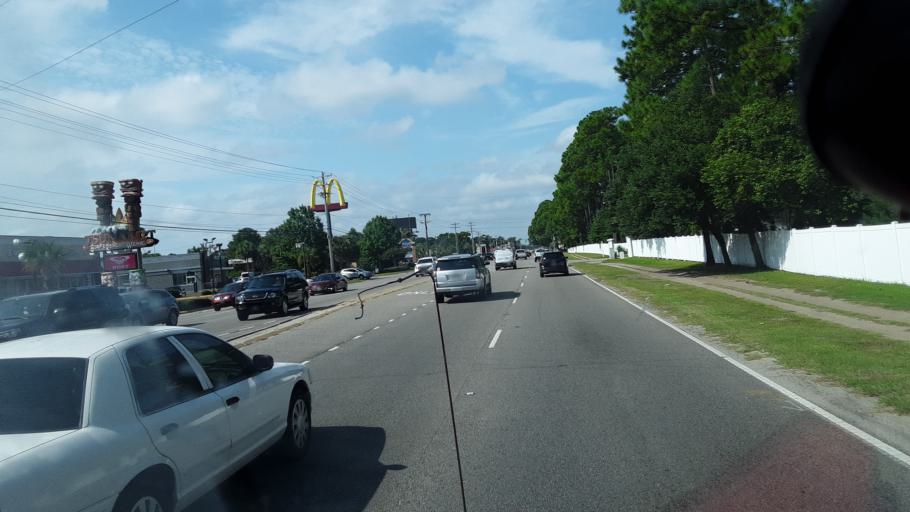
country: US
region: South Carolina
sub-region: Horry County
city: Garden City
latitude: 33.5858
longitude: -79.0128
